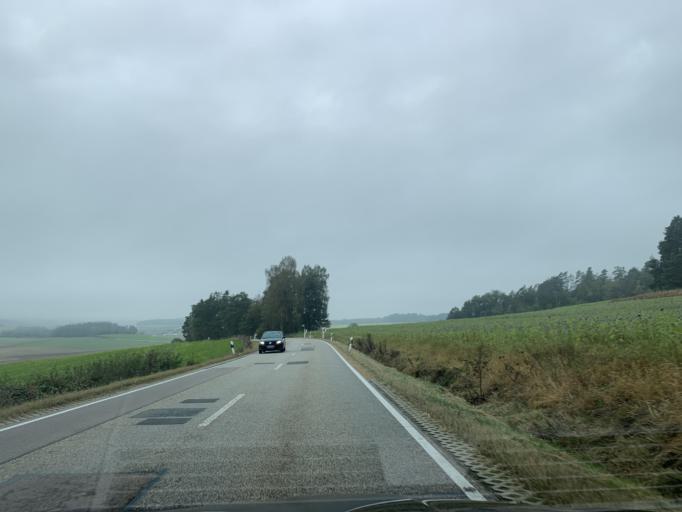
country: DE
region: Bavaria
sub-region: Upper Palatinate
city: Guteneck
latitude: 49.4638
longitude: 12.2734
